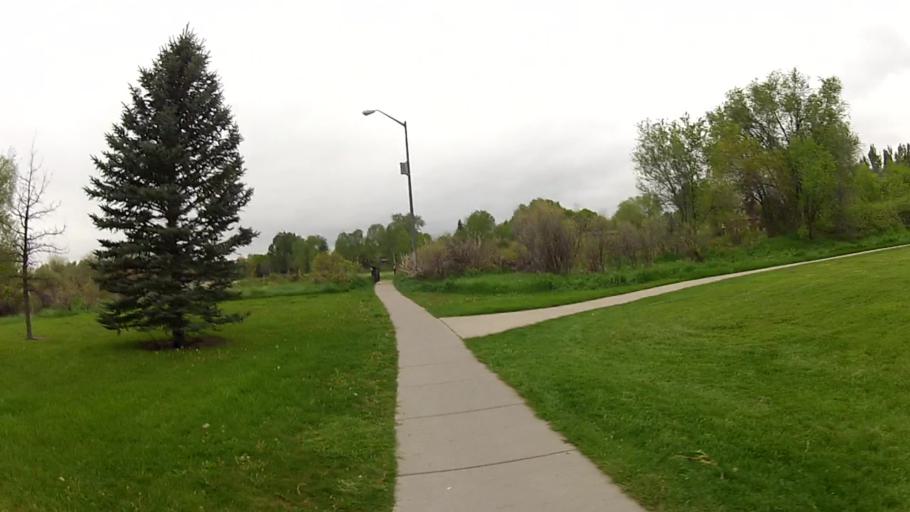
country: US
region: Colorado
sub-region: Larimer County
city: Fort Collins
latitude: 40.5564
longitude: -105.1031
